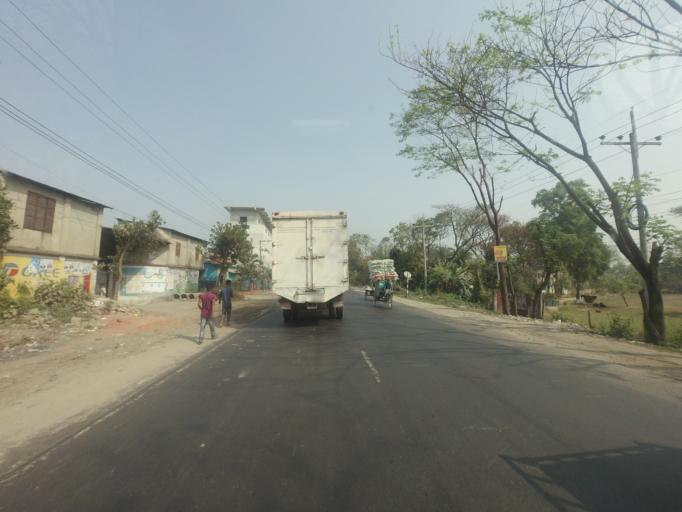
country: BD
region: Dhaka
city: Narsingdi
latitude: 23.8793
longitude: 90.6668
